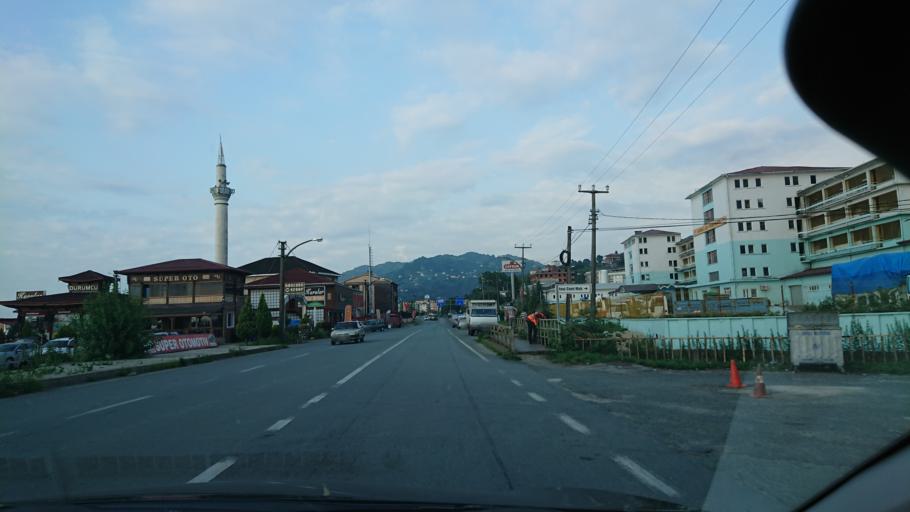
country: TR
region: Rize
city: Cayeli
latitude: 41.0817
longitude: 40.7070
